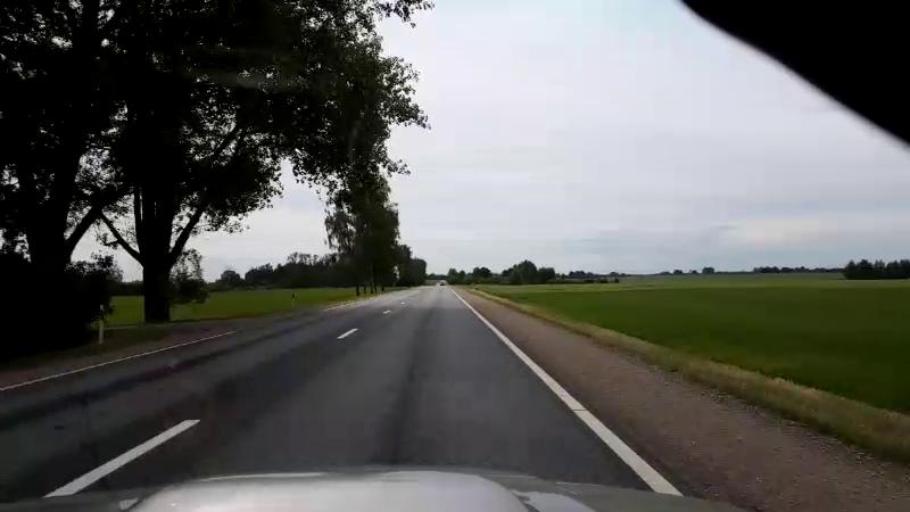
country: LV
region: Lecava
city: Iecava
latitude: 56.5470
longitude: 24.1733
